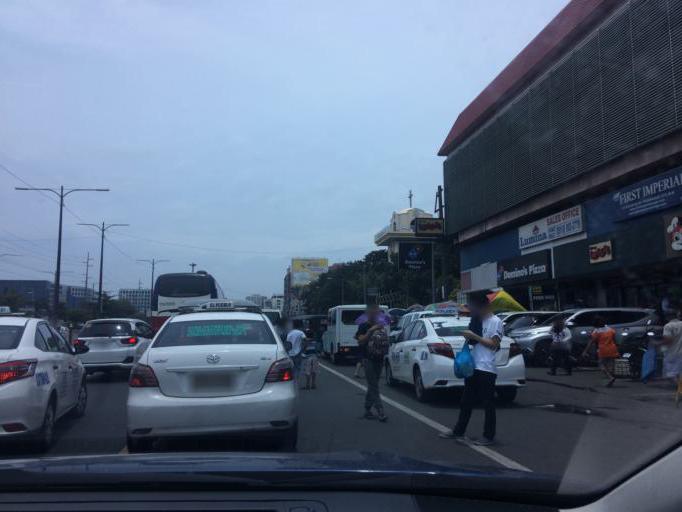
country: PH
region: Metro Manila
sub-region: Makati City
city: Makati City
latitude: 14.5306
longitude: 120.9935
